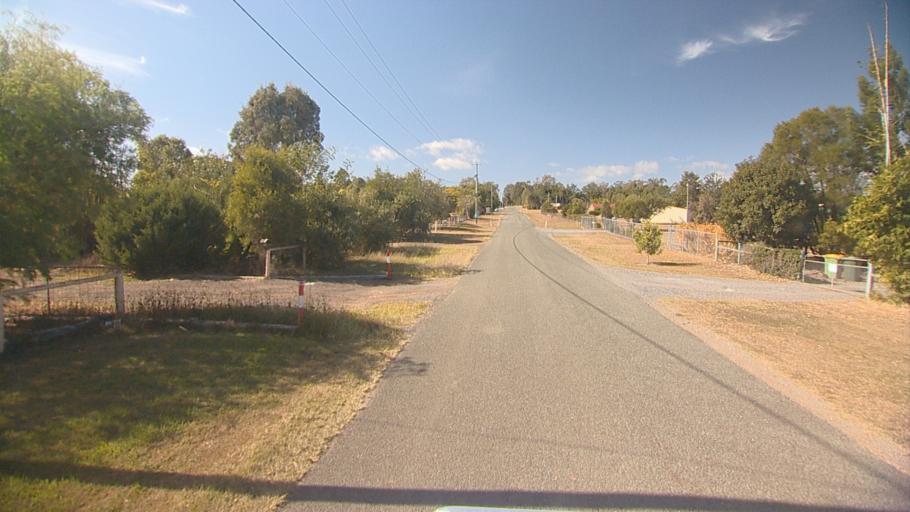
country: AU
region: Queensland
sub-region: Logan
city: Cedar Vale
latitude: -27.8622
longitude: 152.9677
